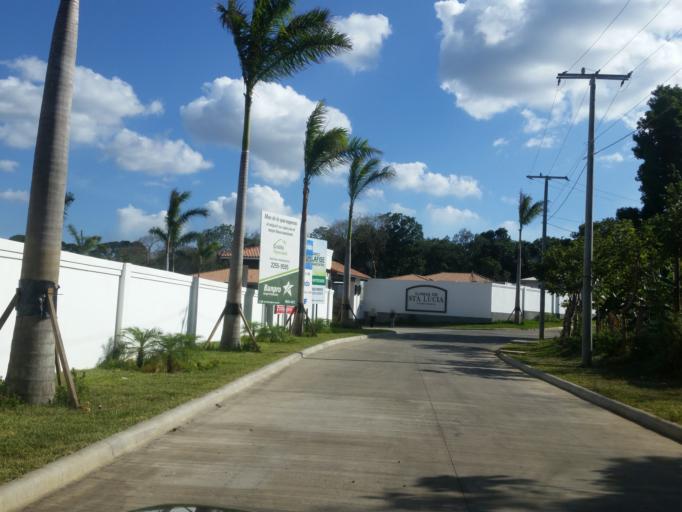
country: NI
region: Managua
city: Managua
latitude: 12.0709
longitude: -86.2458
